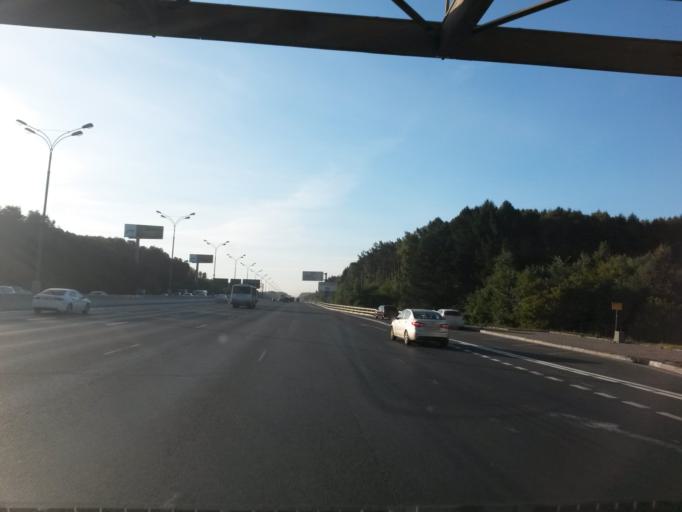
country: RU
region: Moscow
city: Babushkin
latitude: 55.8784
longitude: 37.7331
